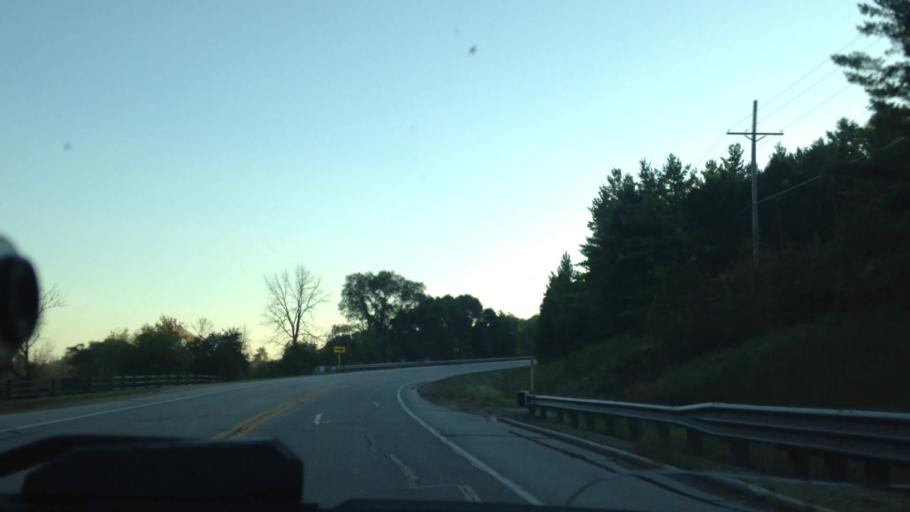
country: US
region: Wisconsin
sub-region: Washington County
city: Newburg
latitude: 43.4258
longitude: -88.0591
